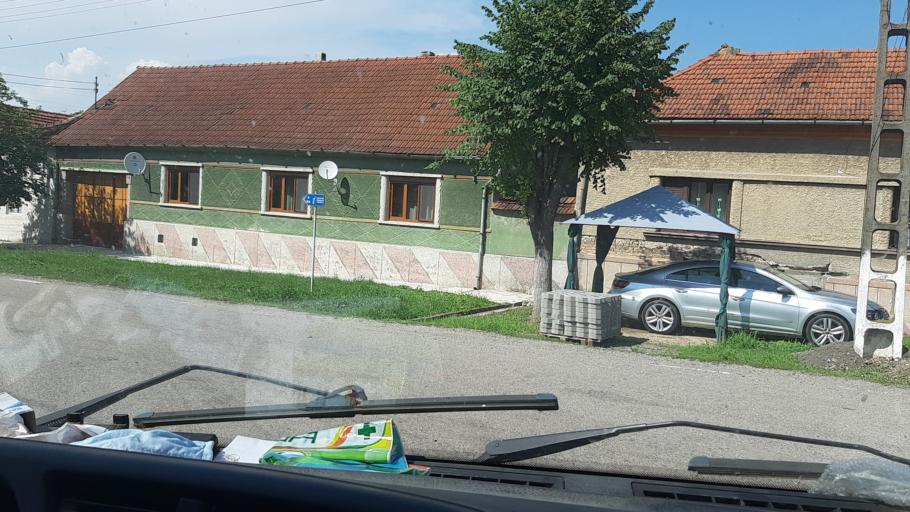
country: RO
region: Caras-Severin
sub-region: Comuna Ezeris
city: Ezeris
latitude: 45.3770
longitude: 21.9404
